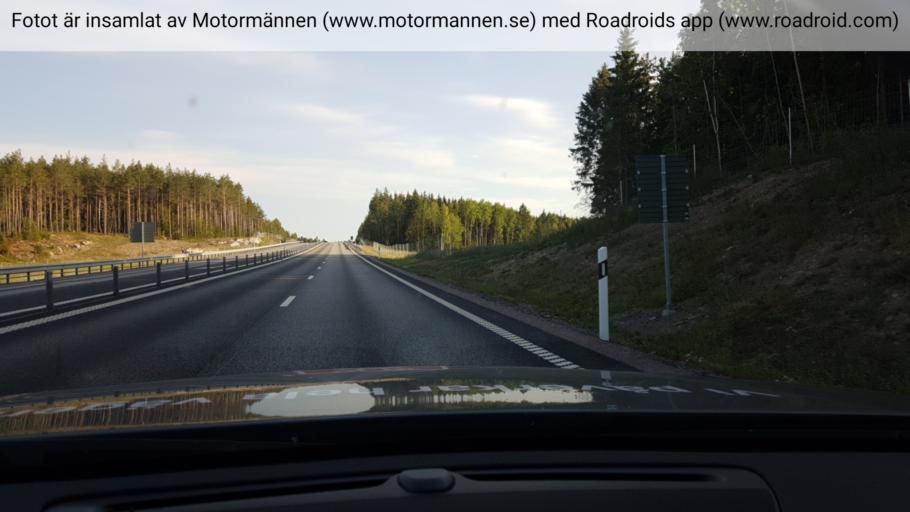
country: SE
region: Uppsala
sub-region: Osthammars Kommun
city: Gimo
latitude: 60.1383
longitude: 18.1566
